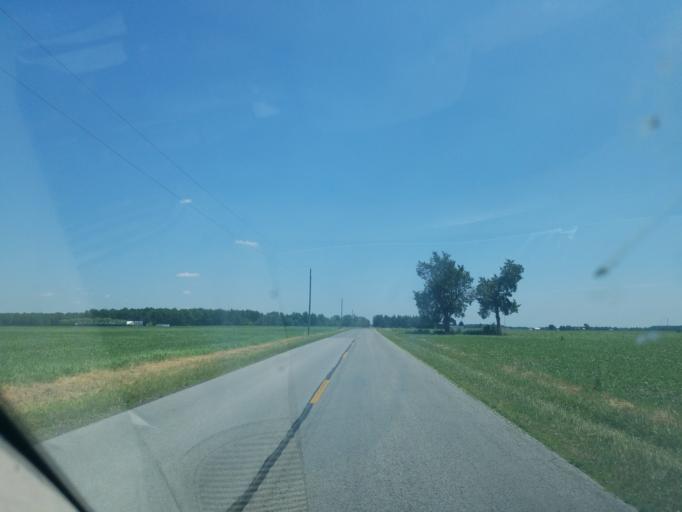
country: US
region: Ohio
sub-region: Allen County
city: Delphos
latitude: 40.7869
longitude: -84.2849
